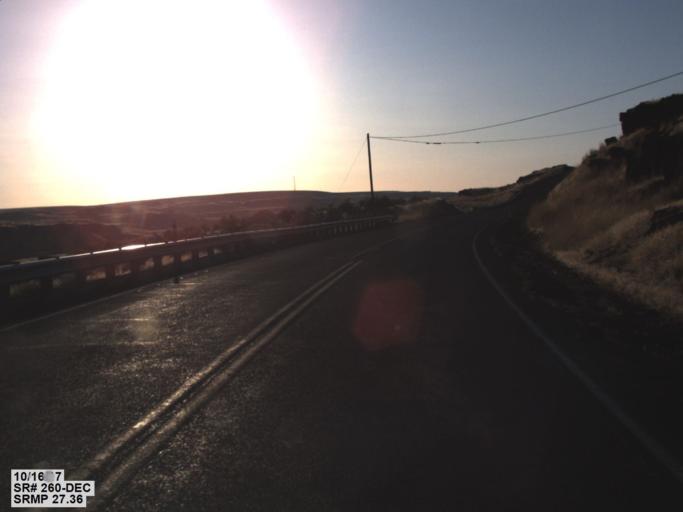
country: US
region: Washington
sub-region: Franklin County
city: Connell
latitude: 46.6506
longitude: -118.5047
